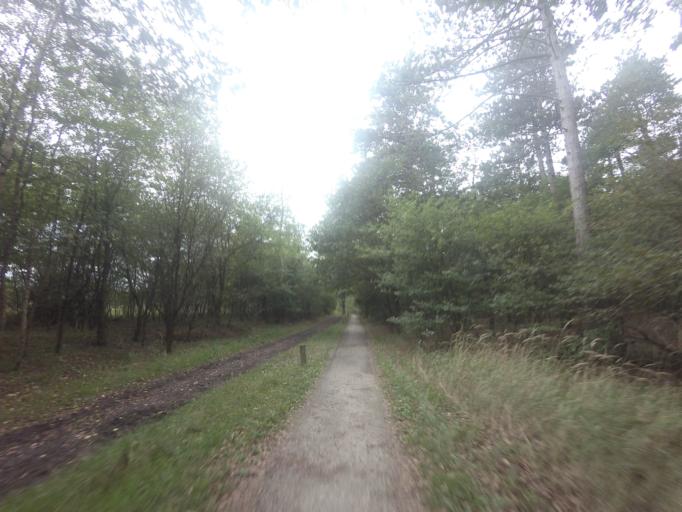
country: NL
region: Drenthe
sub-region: Gemeente Westerveld
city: Dwingeloo
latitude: 52.9271
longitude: 6.3337
